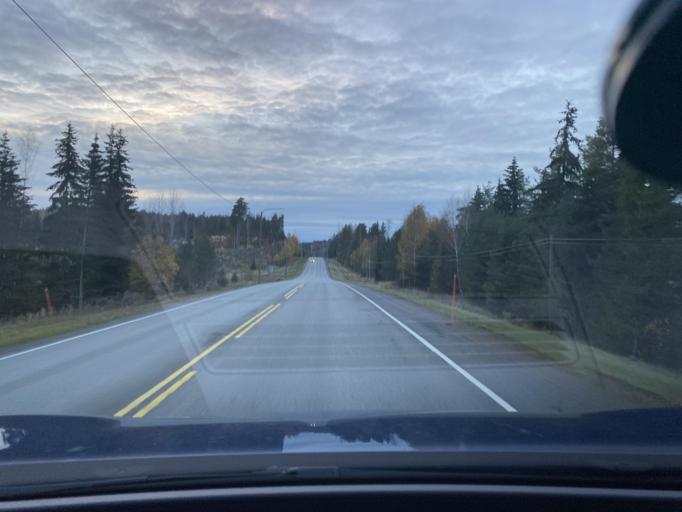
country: FI
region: Uusimaa
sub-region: Helsinki
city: Saukkola
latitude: 60.3850
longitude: 24.0786
